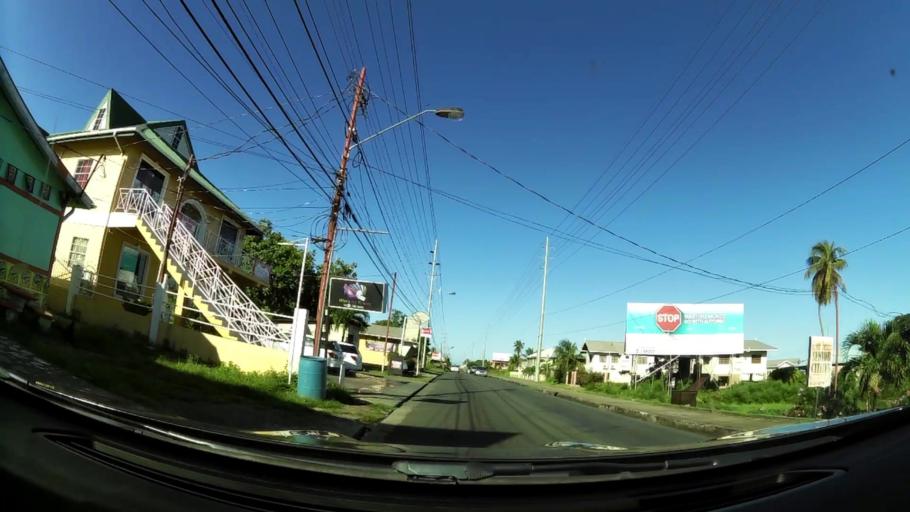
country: TT
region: Tobago
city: Scarborough
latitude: 11.1578
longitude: -60.8245
